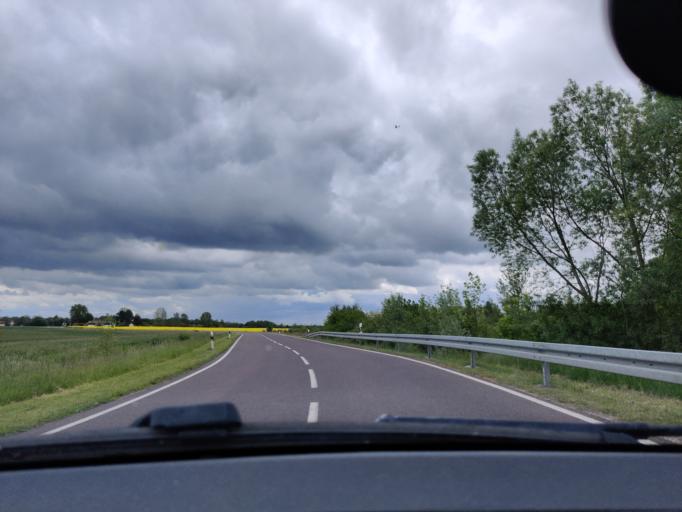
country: DE
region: Saxony-Anhalt
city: Schonebeck
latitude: 51.9824
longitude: 11.7628
